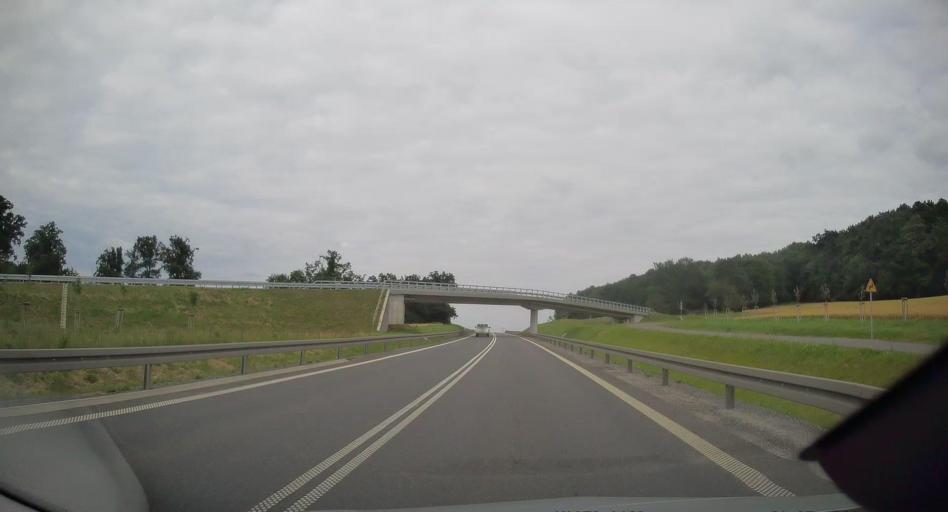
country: PL
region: Lower Silesian Voivodeship
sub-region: Powiat jaworski
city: Bolkow
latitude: 50.9114
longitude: 16.0982
